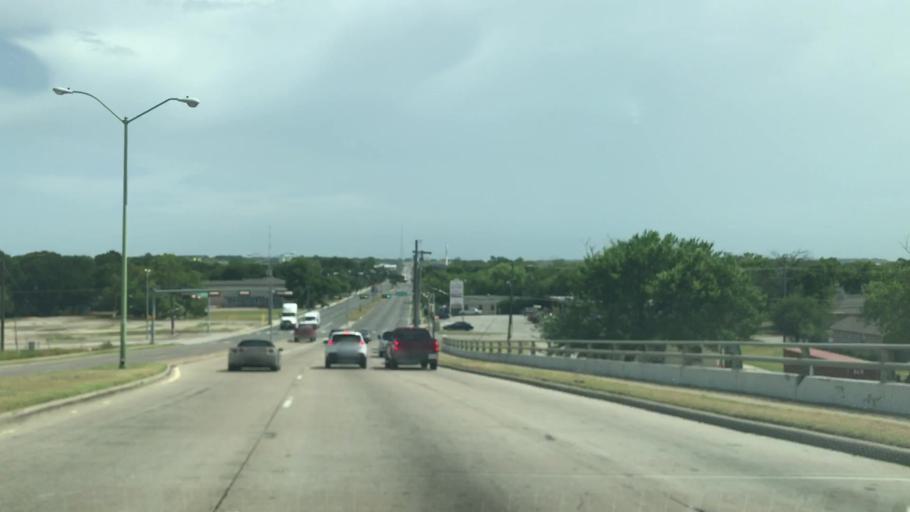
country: US
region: Texas
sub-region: Dallas County
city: Cockrell Hill
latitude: 32.7936
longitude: -96.8739
